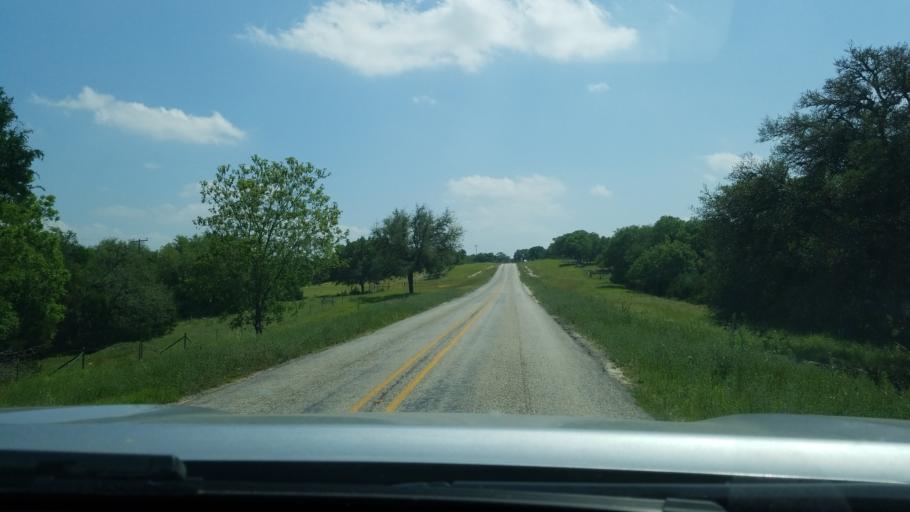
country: US
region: Texas
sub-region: Blanco County
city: Blanco
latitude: 29.9467
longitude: -98.5646
